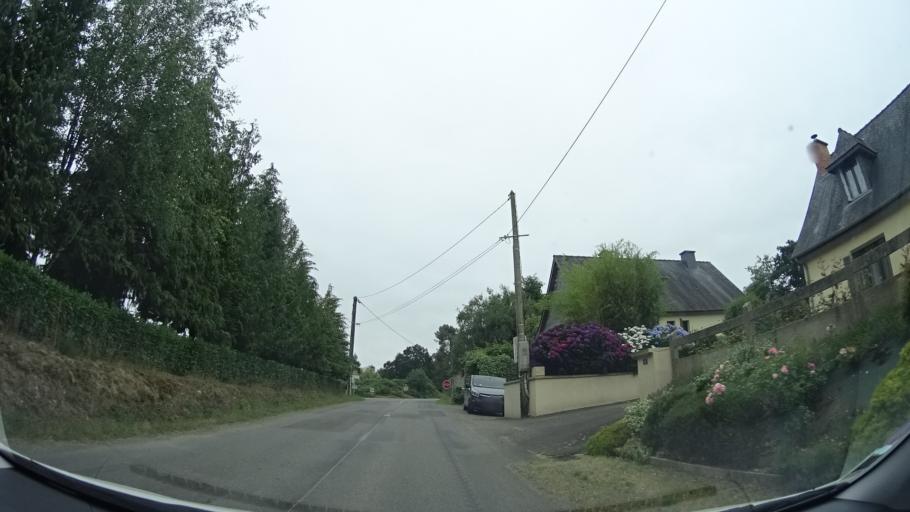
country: FR
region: Brittany
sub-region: Departement d'Ille-et-Vilaine
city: Hede-Bazouges
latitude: 48.2992
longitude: -1.7676
